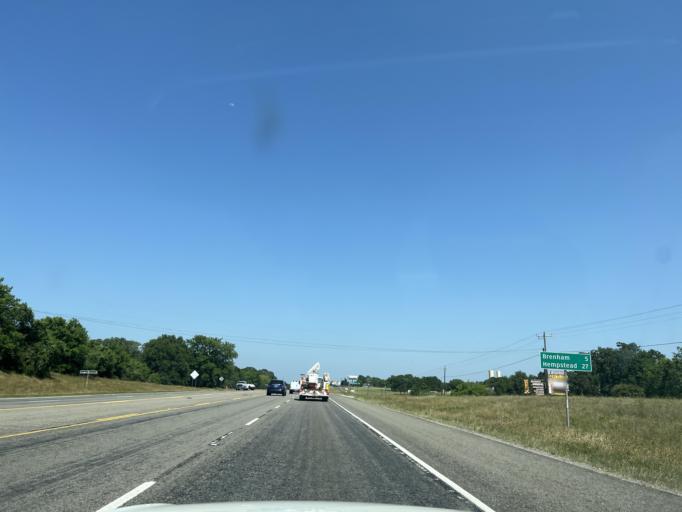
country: US
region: Texas
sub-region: Washington County
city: Brenham
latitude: 30.1795
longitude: -96.4724
